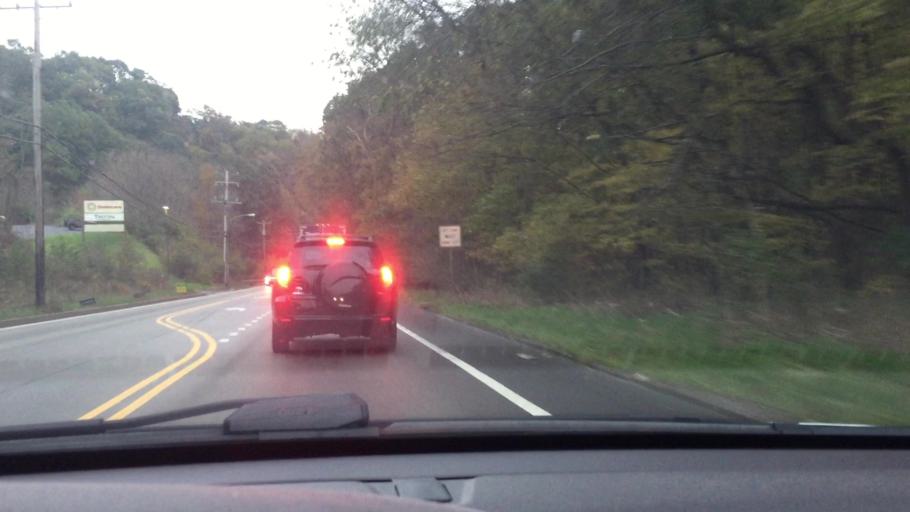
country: US
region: Pennsylvania
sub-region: Allegheny County
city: Ingram
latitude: 40.4478
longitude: -80.1035
